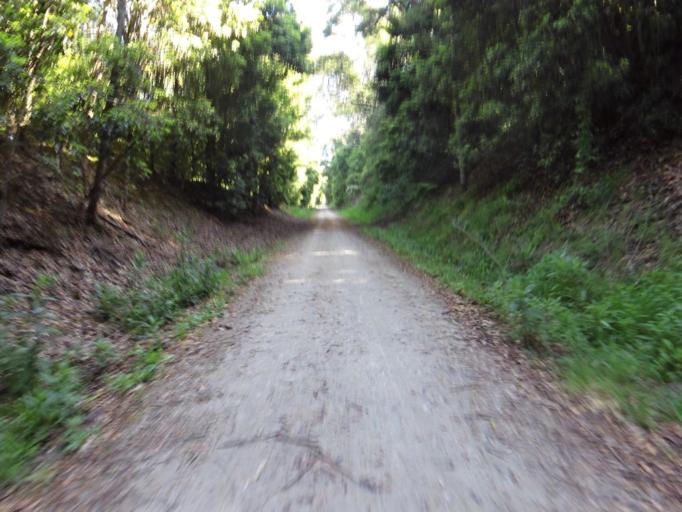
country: AU
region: Victoria
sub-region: Latrobe
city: Morwell
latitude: -38.6779
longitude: 146.1604
